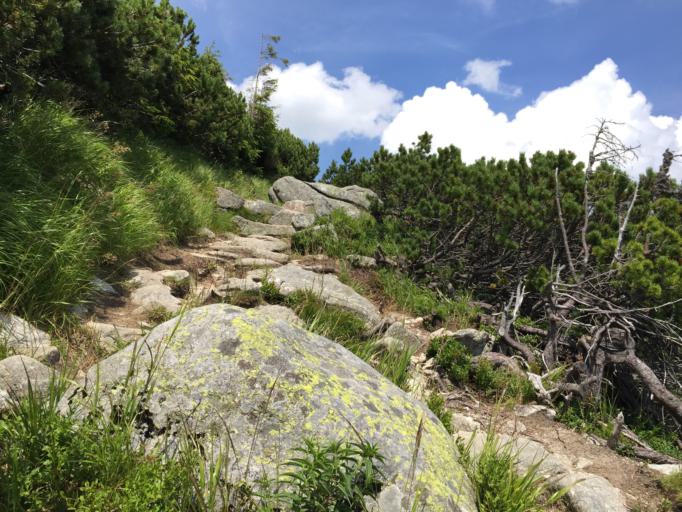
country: SK
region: Presovsky
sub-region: Okres Poprad
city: Vysoke Tatry
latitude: 49.1625
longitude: 20.2132
